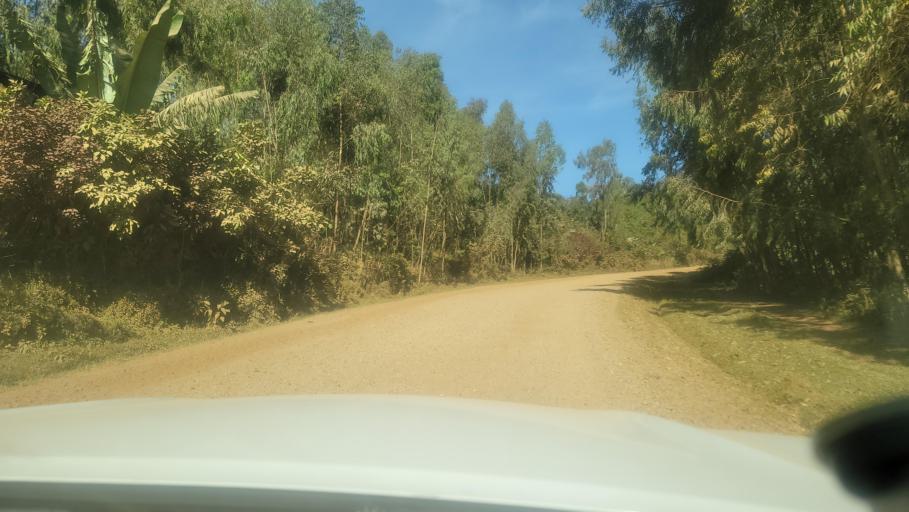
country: ET
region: Oromiya
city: Agaro
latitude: 7.8005
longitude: 36.4665
